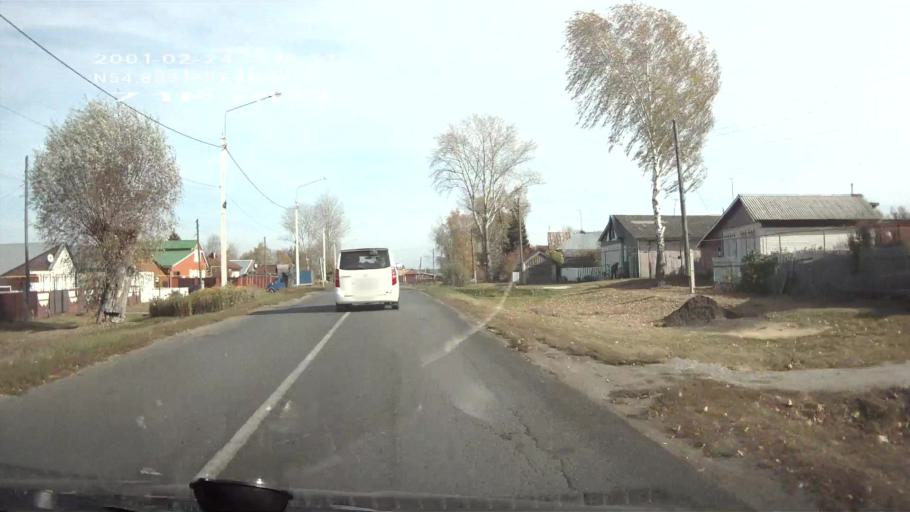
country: RU
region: Mordoviya
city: Turgenevo
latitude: 54.8532
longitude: 46.3973
